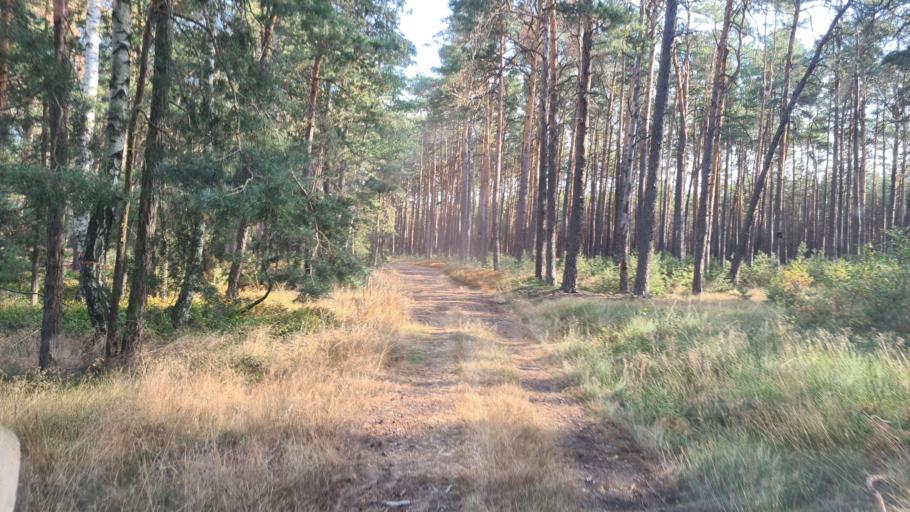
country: DE
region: Brandenburg
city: Crinitz
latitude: 51.6766
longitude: 13.7532
